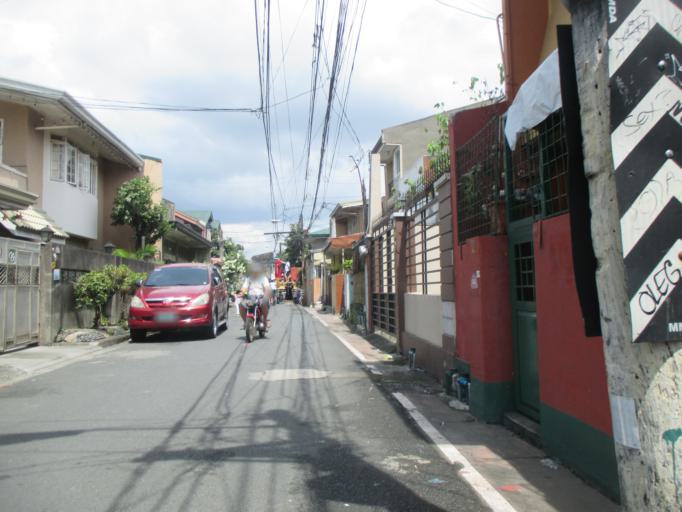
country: PH
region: Metro Manila
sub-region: Marikina
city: Calumpang
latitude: 14.6287
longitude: 121.0971
